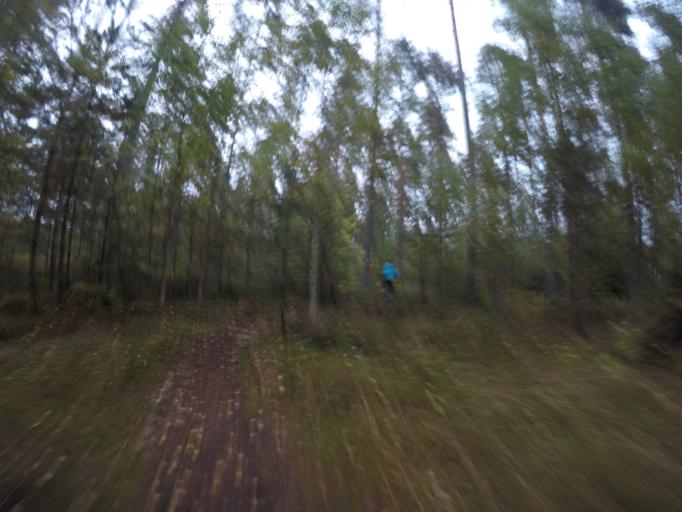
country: SE
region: Vaestmanland
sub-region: Kungsors Kommun
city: Kungsoer
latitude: 59.3752
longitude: 16.1182
